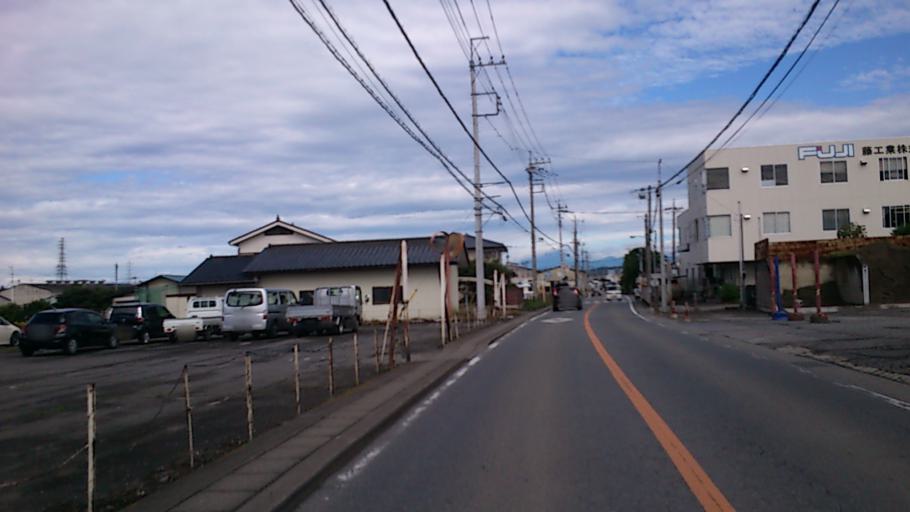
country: JP
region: Gunma
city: Fujioka
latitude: 36.2612
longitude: 139.0825
